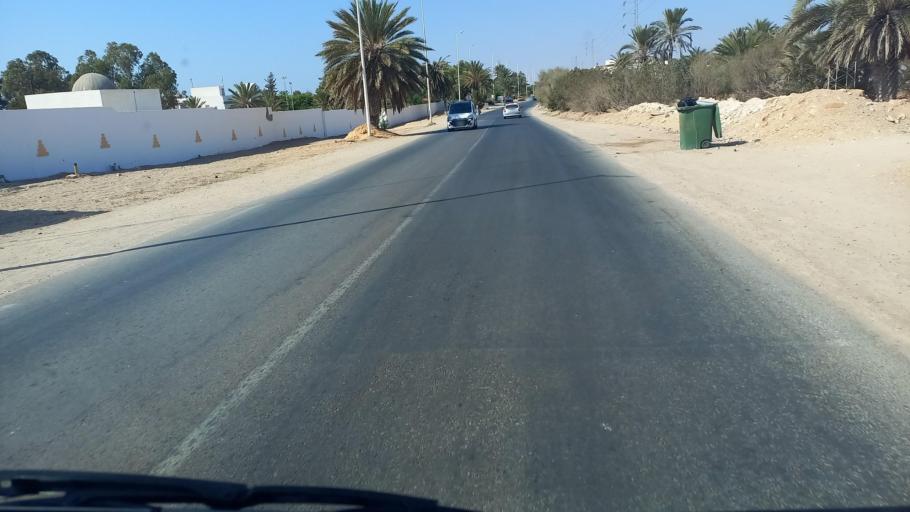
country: TN
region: Madanin
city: Midoun
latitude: 33.7803
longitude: 11.0424
